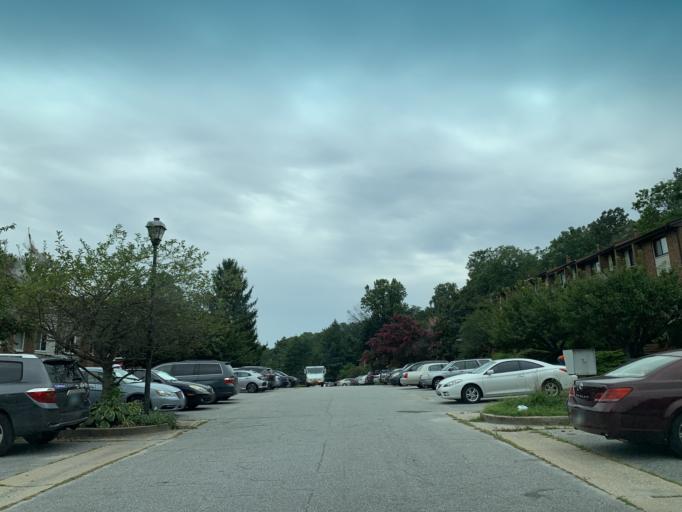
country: US
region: Maryland
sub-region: Baltimore County
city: Carney
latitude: 39.4156
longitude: -76.5331
